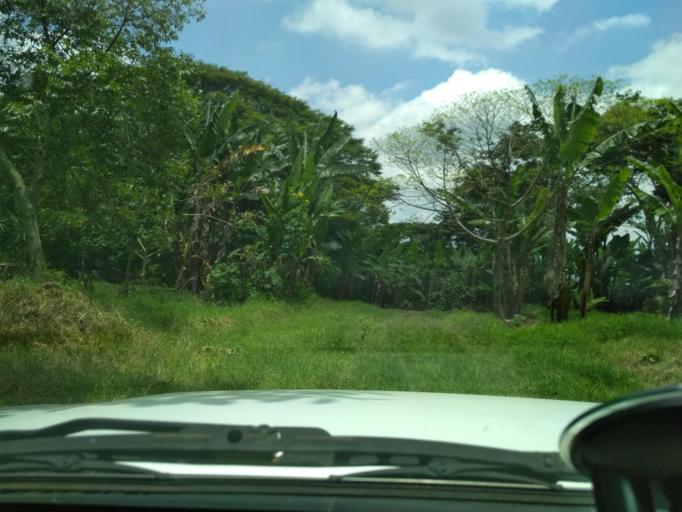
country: MX
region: Veracruz
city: Tocuila
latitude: 18.9457
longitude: -97.0147
